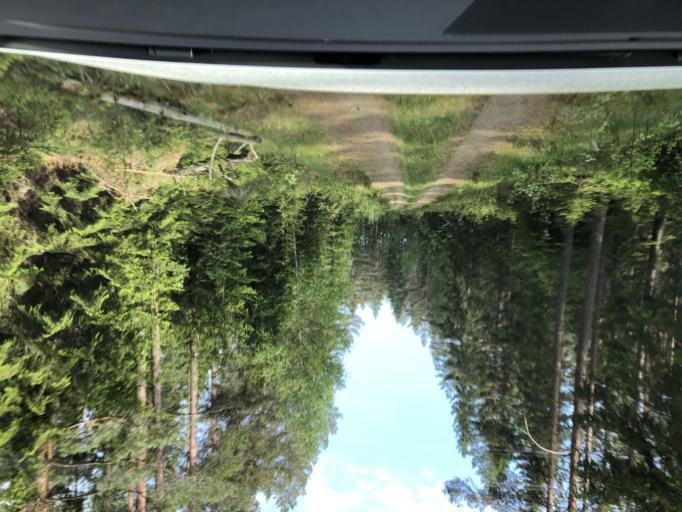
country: SE
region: Dalarna
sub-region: Avesta Kommun
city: Horndal
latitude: 60.2158
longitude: 16.5114
